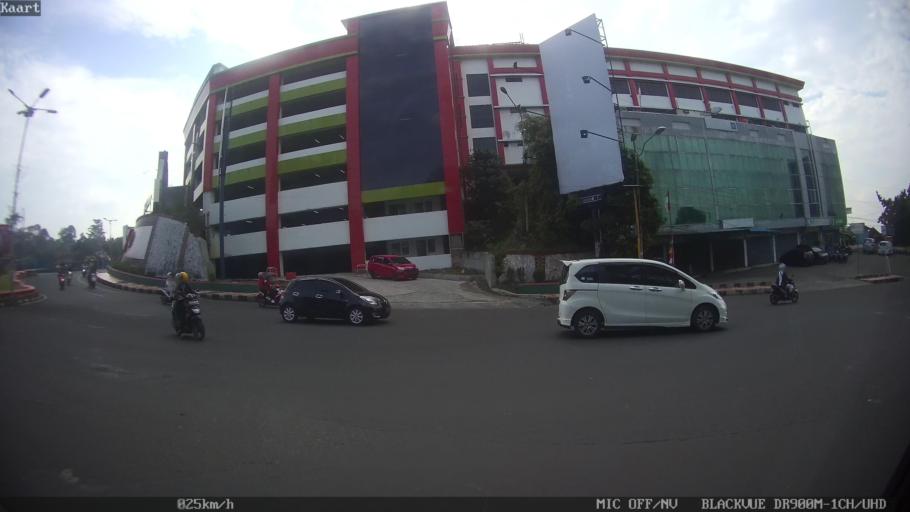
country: ID
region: Lampung
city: Bandarlampung
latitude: -5.4299
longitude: 105.2614
